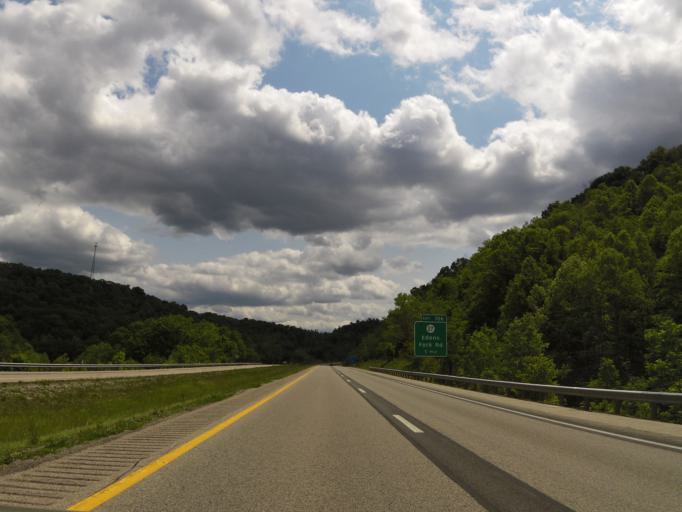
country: US
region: West Virginia
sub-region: Kanawha County
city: Charleston
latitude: 38.4306
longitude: -81.6251
